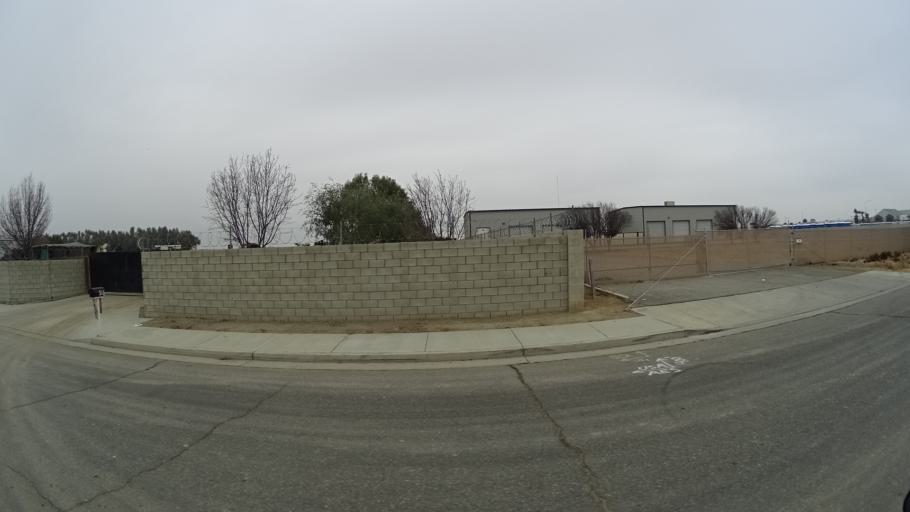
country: US
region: California
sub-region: Kern County
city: Bakersfield
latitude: 35.3503
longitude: -118.9531
